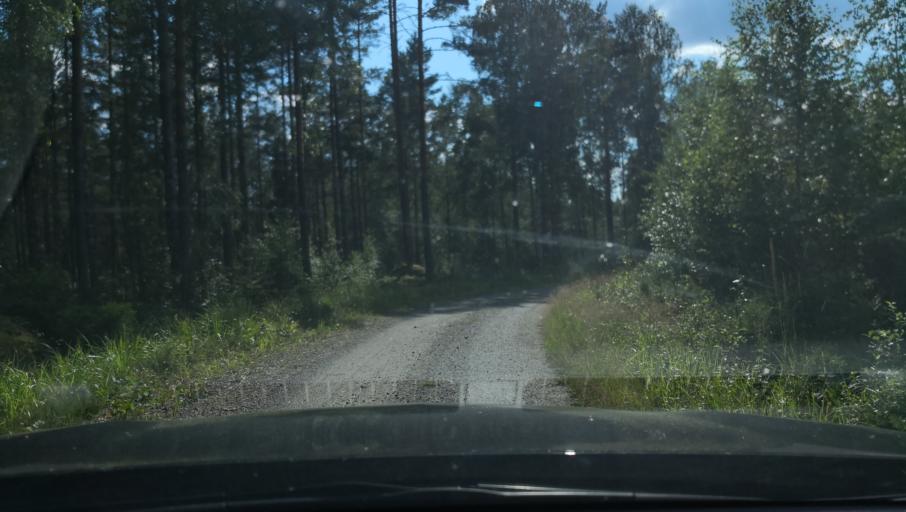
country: SE
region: Vaestmanland
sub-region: Vasteras
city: Skultuna
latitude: 59.7239
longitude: 16.3499
